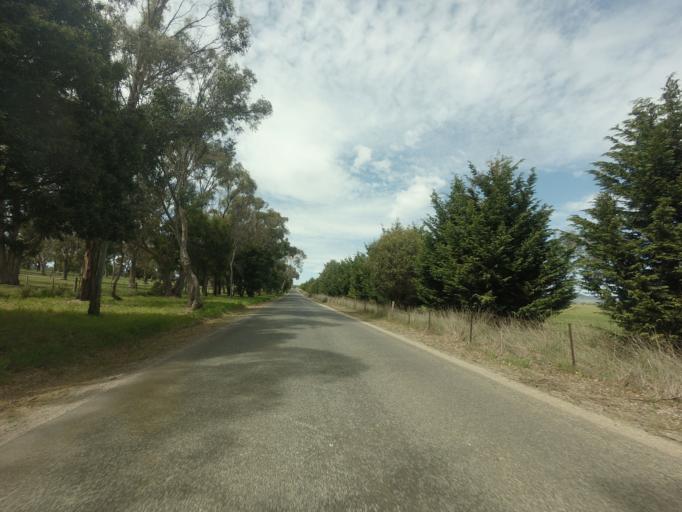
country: AU
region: Tasmania
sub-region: Northern Midlands
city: Longford
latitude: -41.6617
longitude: 147.1777
